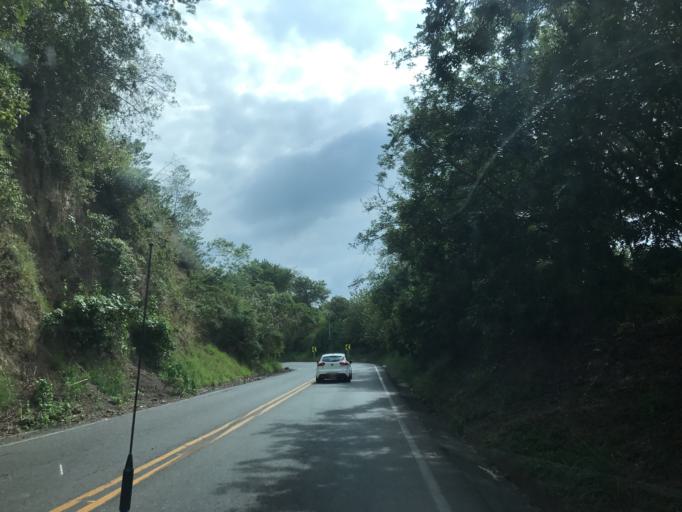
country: CO
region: Valle del Cauca
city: Cartago
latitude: 4.7355
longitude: -75.8961
